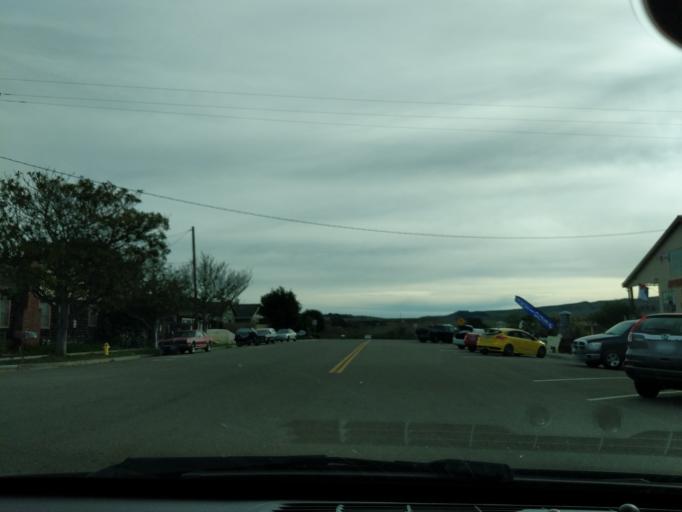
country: US
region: California
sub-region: Santa Barbara County
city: Orcutt
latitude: 34.8632
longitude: -120.4473
